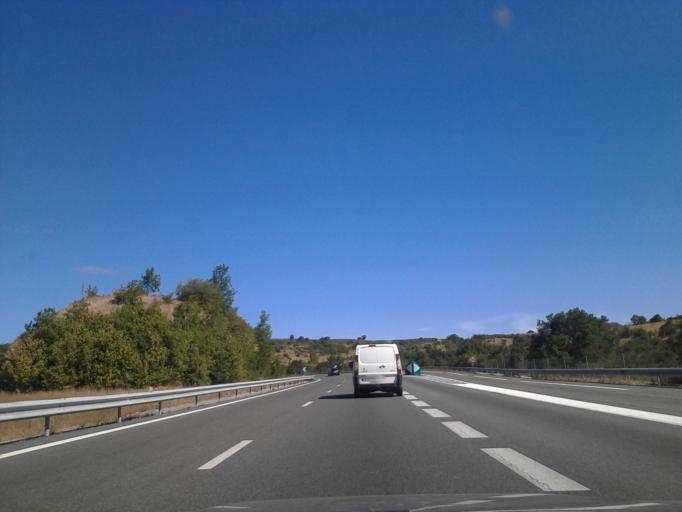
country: FR
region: Languedoc-Roussillon
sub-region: Departement de l'Herault
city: Lodeve
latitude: 43.8444
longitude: 3.3121
